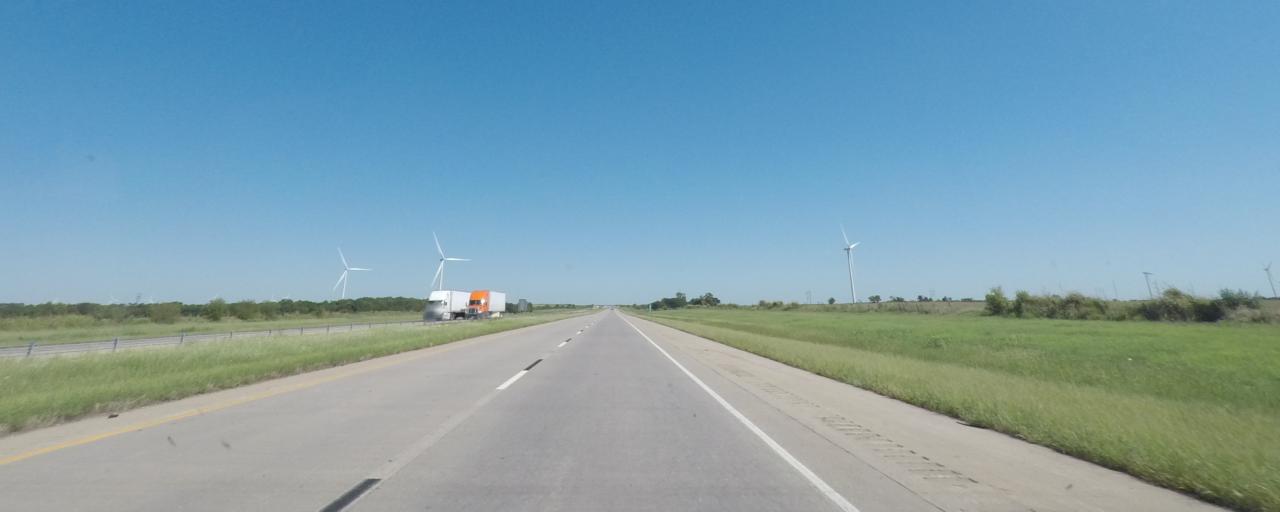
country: US
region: Oklahoma
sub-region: Kay County
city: Tonkawa
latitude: 36.5509
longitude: -97.3455
